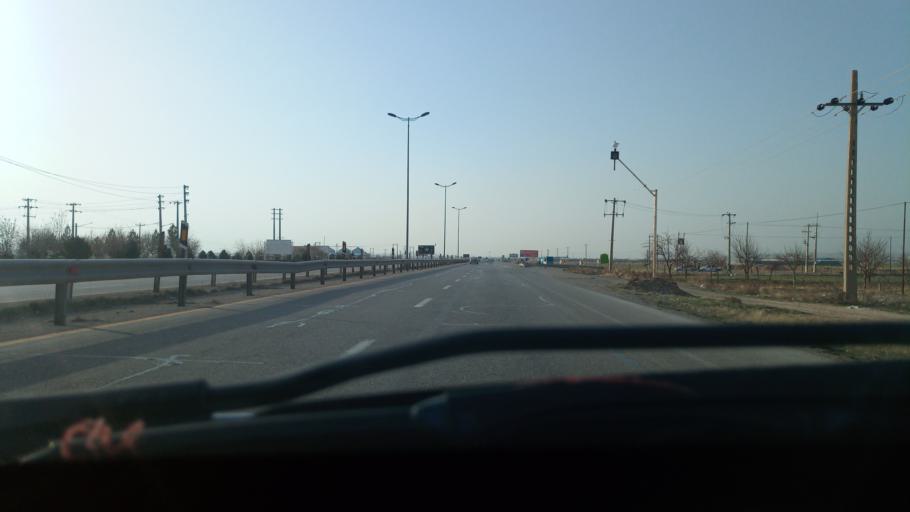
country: IR
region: Khorasan-e Shomali
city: Faruj
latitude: 37.2418
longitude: 58.2068
